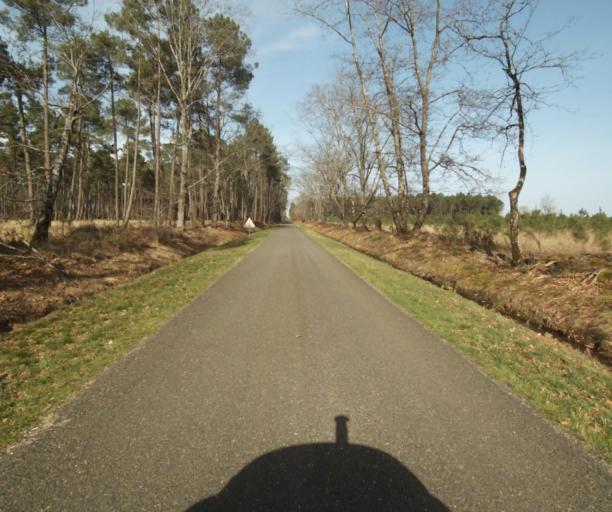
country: FR
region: Aquitaine
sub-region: Departement des Landes
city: Roquefort
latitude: 44.1553
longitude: -0.1699
